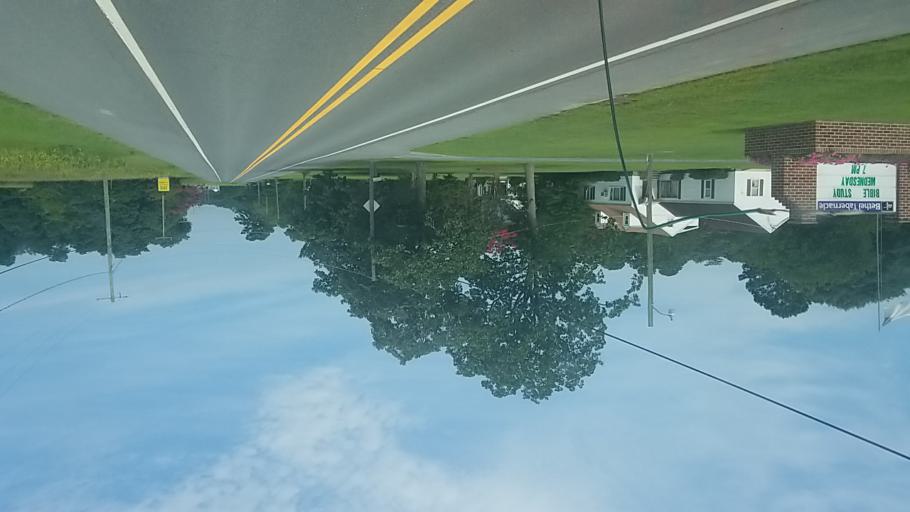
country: US
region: Delaware
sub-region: Sussex County
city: Ocean View
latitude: 38.5480
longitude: -75.1523
